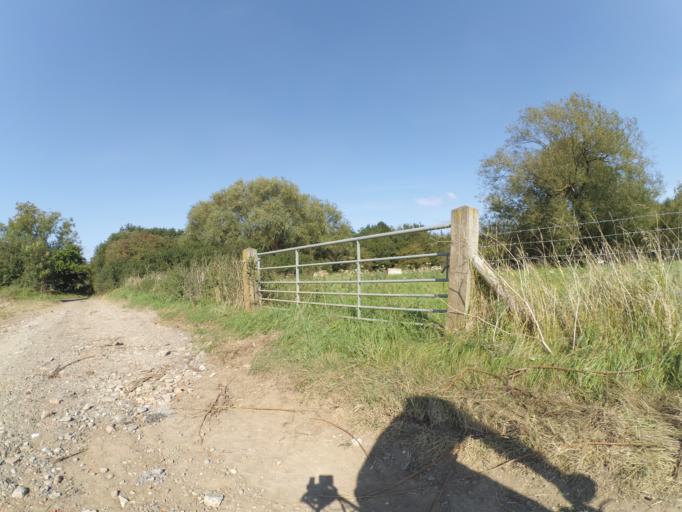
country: GB
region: England
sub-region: Warwickshire
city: Rugby
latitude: 52.4154
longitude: -1.2650
